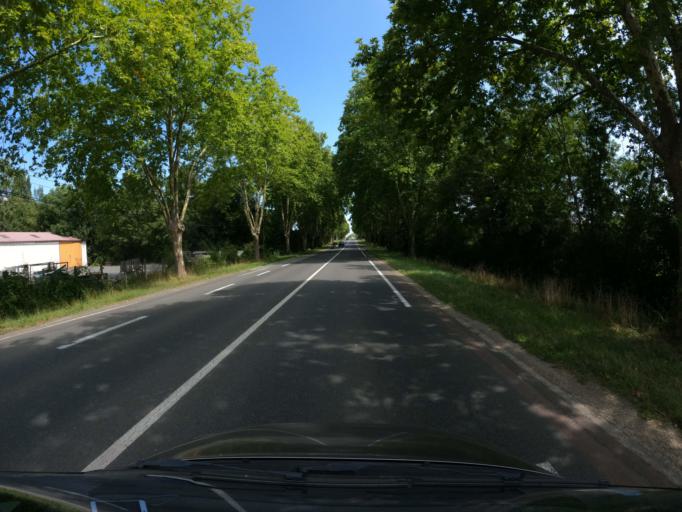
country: FR
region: Poitou-Charentes
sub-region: Departement des Deux-Sevres
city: Bessines
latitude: 46.2933
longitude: -0.5044
